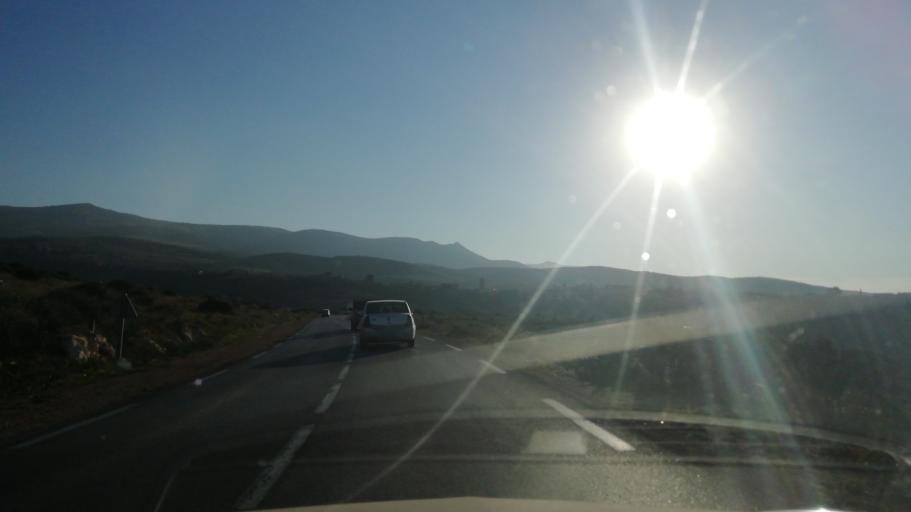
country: DZ
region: Tlemcen
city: Beni Mester
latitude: 34.8468
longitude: -1.4658
